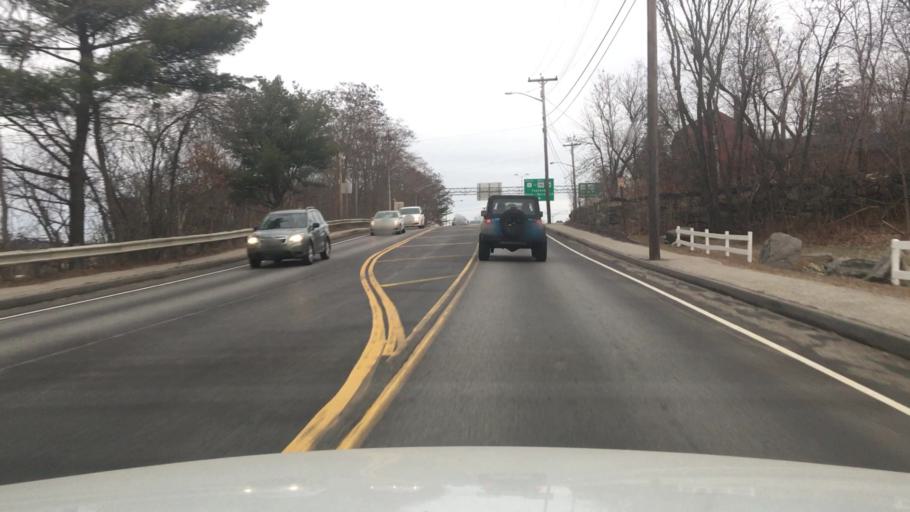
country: US
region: Maine
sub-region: Cumberland County
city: Brunswick
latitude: 43.9173
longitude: -69.9714
